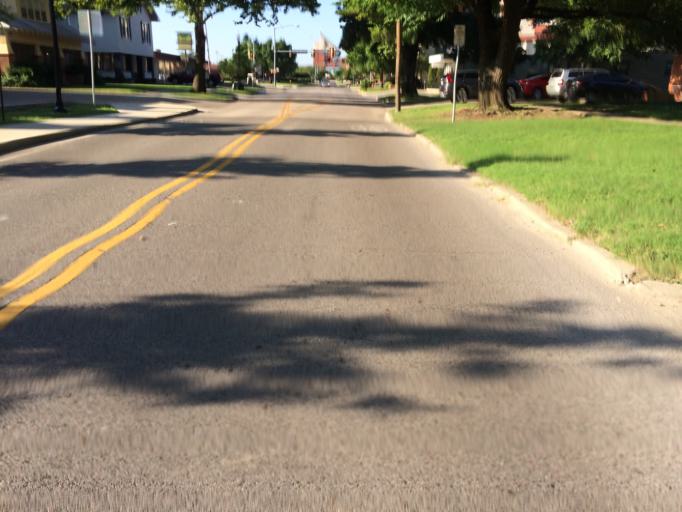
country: US
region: Oklahoma
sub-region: Cleveland County
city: Norman
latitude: 35.2122
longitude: -97.4413
